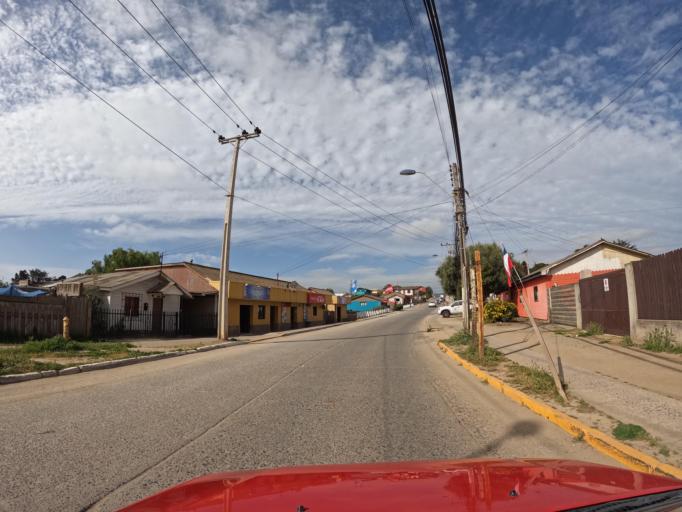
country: CL
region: O'Higgins
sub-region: Provincia de Colchagua
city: Santa Cruz
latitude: -34.3877
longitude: -72.0000
